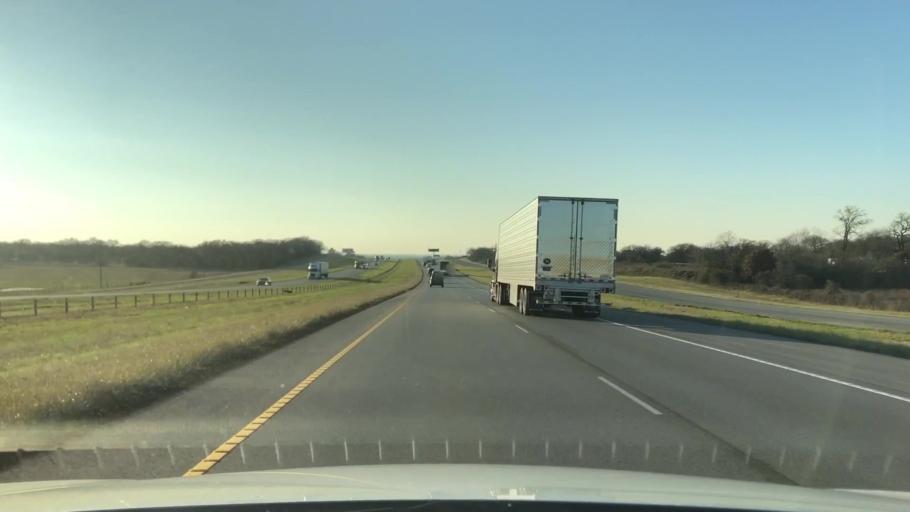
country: US
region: Texas
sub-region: Caldwell County
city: Luling
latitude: 29.6544
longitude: -97.5611
